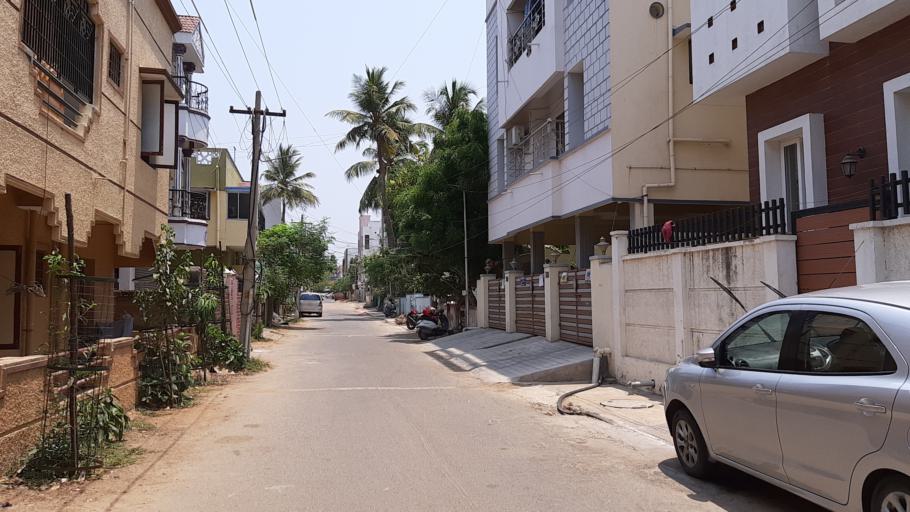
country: IN
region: Tamil Nadu
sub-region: Kancheepuram
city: Manappakkam
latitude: 13.0282
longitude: 80.1862
